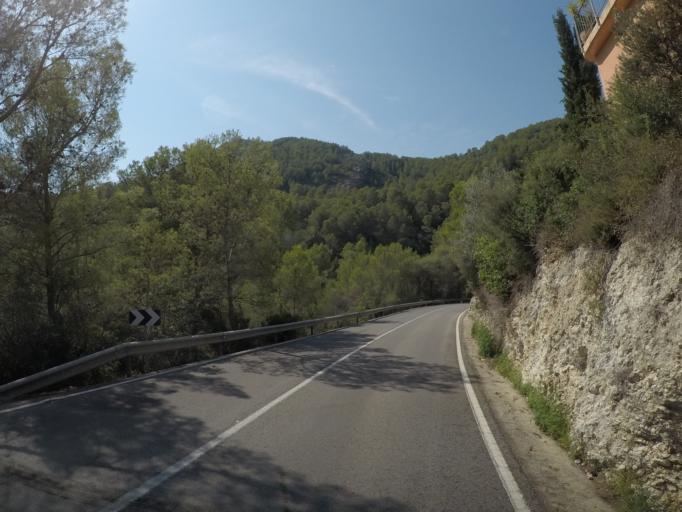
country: ES
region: Valencia
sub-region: Provincia de Alicante
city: Orba
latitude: 38.7805
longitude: -0.0789
